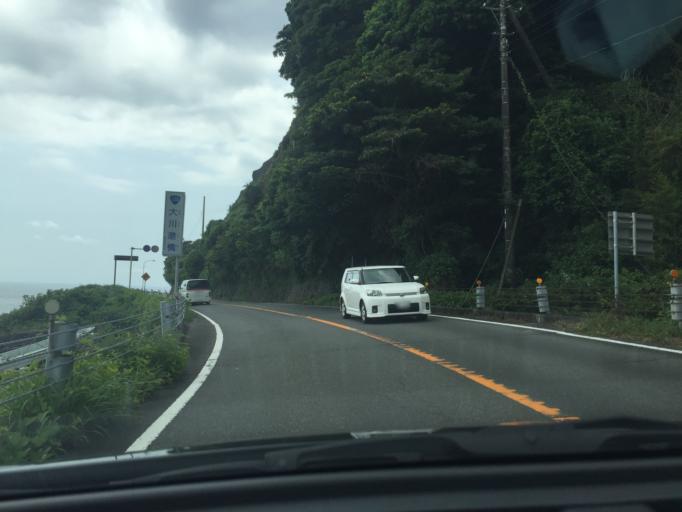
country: JP
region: Shizuoka
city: Ito
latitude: 34.8403
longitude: 139.0767
